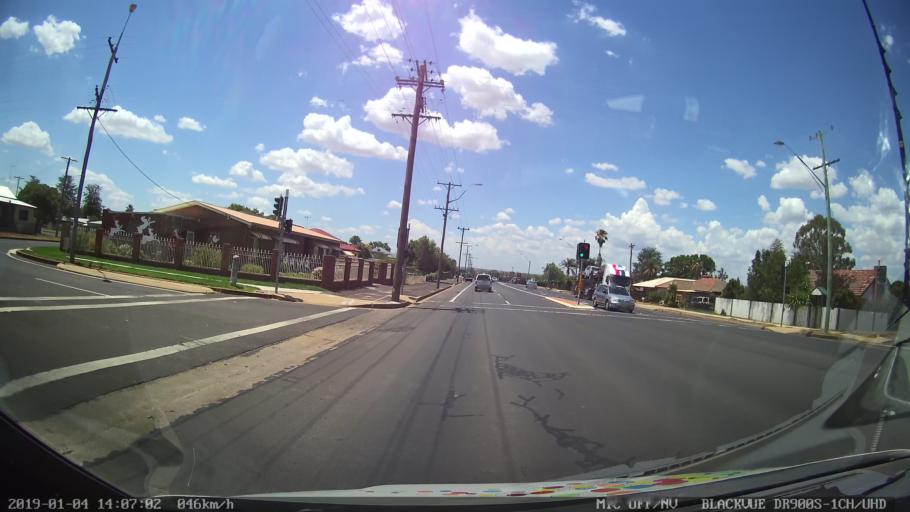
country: AU
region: New South Wales
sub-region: Dubbo Municipality
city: Dubbo
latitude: -32.2514
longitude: 148.5906
